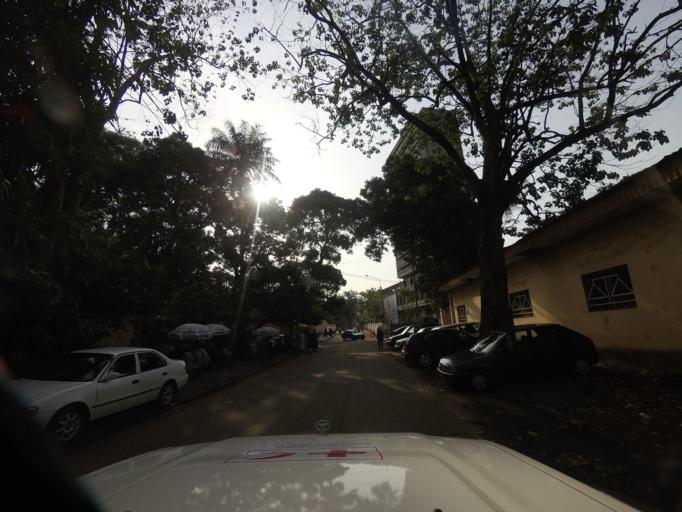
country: GN
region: Conakry
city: Camayenne
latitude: 9.5118
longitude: -13.7173
